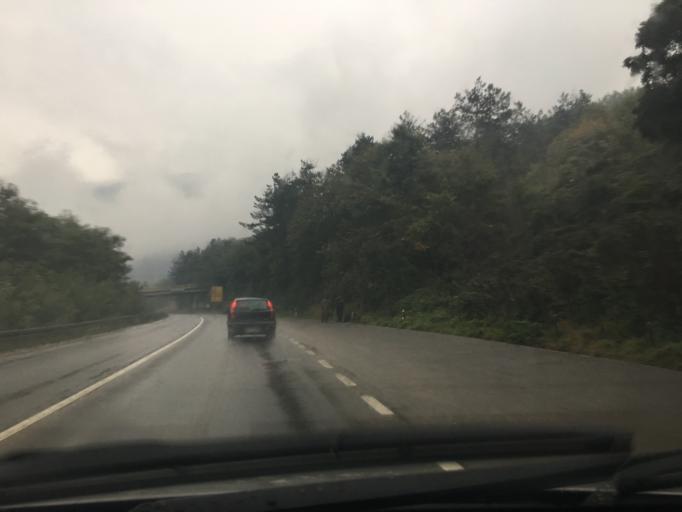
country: RS
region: Central Serbia
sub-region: Pcinjski Okrug
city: Vladicin Han
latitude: 42.7716
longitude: 22.0889
